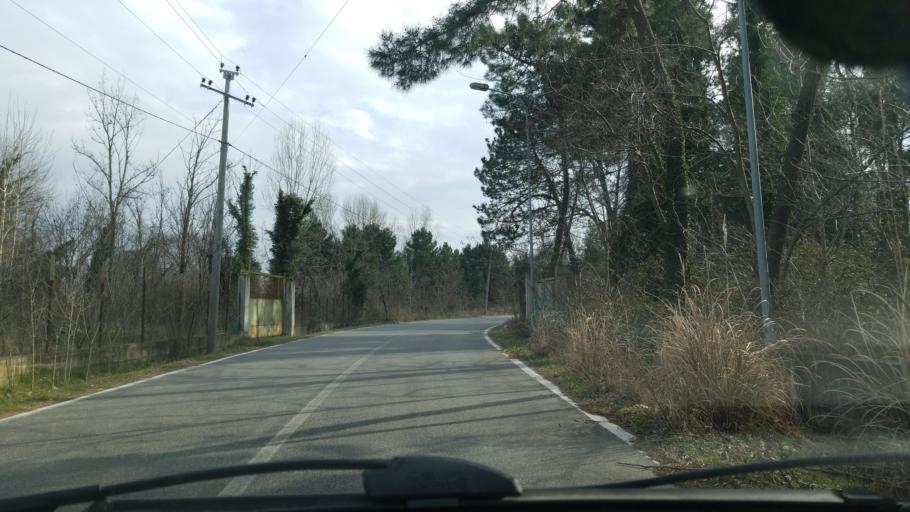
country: AL
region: Lezhe
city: Shengjin
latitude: 41.7816
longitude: 19.6039
